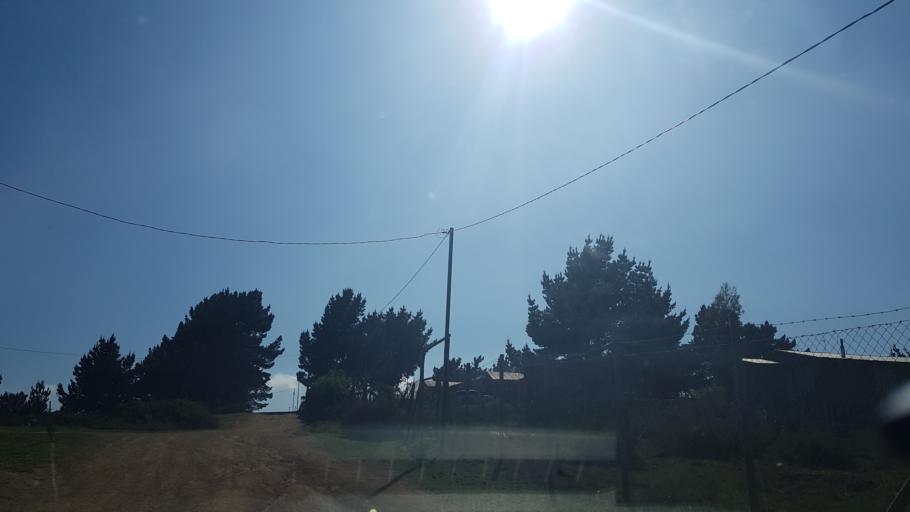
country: CL
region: Valparaiso
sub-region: Provincia de Valparaiso
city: Valparaiso
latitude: -33.1371
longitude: -71.6585
